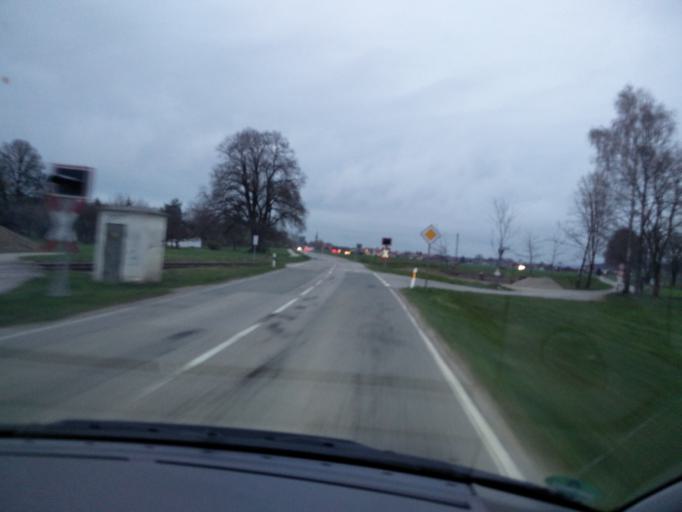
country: DE
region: Bavaria
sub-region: Upper Bavaria
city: Halfing
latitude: 47.9401
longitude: 12.2806
